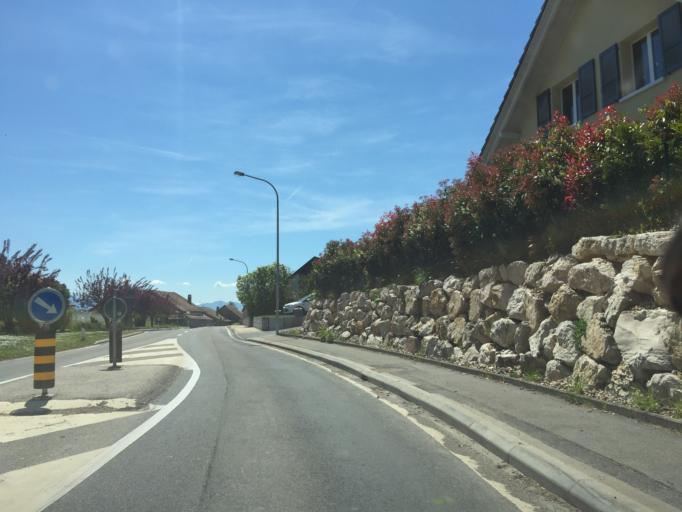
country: CH
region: Vaud
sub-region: Morges District
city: Grancy
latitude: 46.5764
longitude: 6.4547
